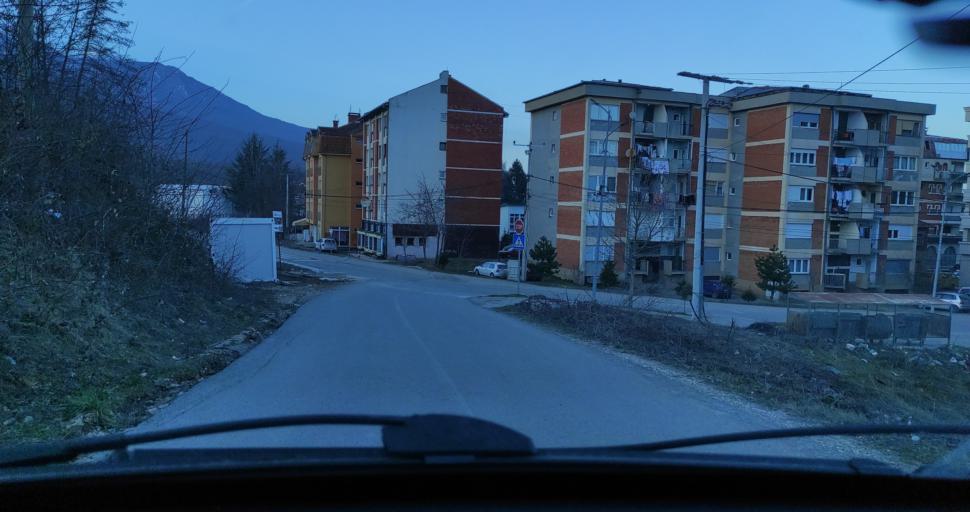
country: XK
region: Gjakova
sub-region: Komuna e Decanit
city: Decan
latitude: 42.5393
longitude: 20.2852
